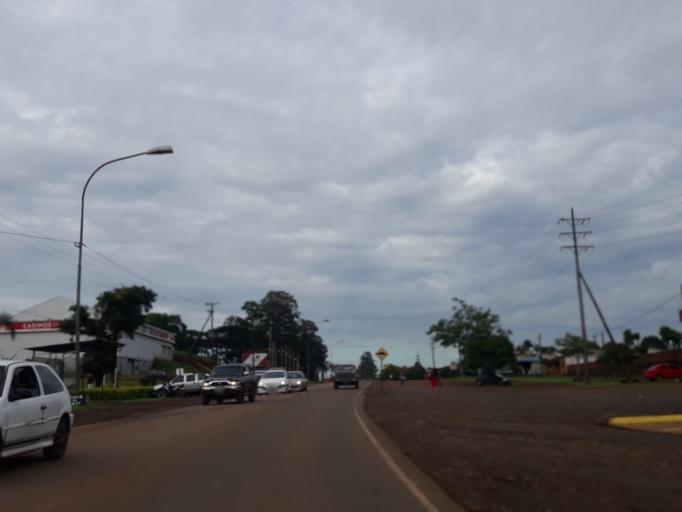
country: AR
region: Misiones
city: Bernardo de Irigoyen
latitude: -26.2610
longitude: -53.6483
